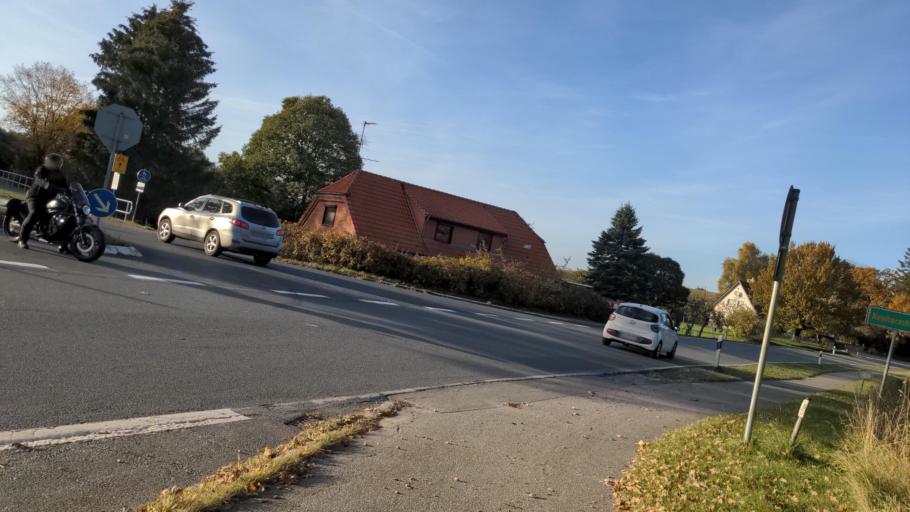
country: DE
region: Schleswig-Holstein
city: Kirchnuchel
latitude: 54.2070
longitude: 10.6729
